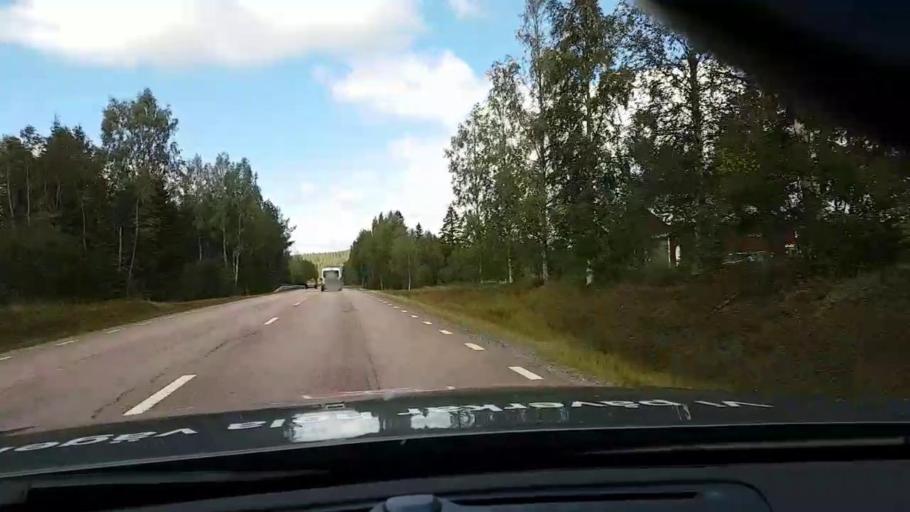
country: SE
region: Vaesternorrland
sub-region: OErnskoeldsviks Kommun
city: Bjasta
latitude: 63.3743
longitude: 18.4319
